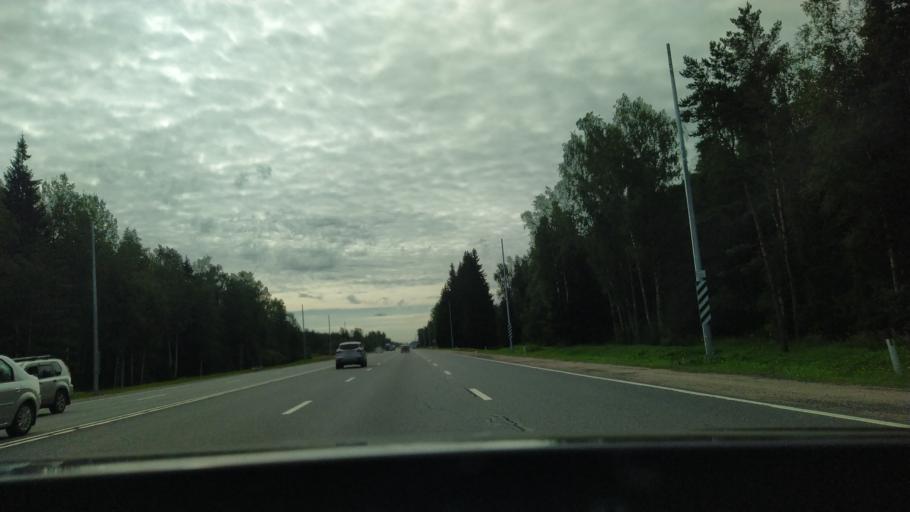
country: RU
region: Leningrad
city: Ul'yanovka
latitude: 59.5819
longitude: 30.8026
